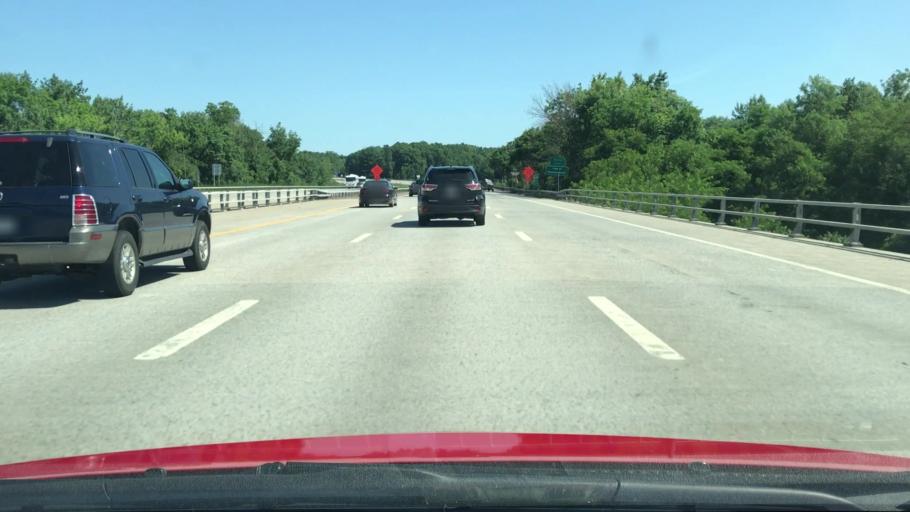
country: US
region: New York
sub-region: Warren County
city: West Glens Falls
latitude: 43.2641
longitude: -73.6757
